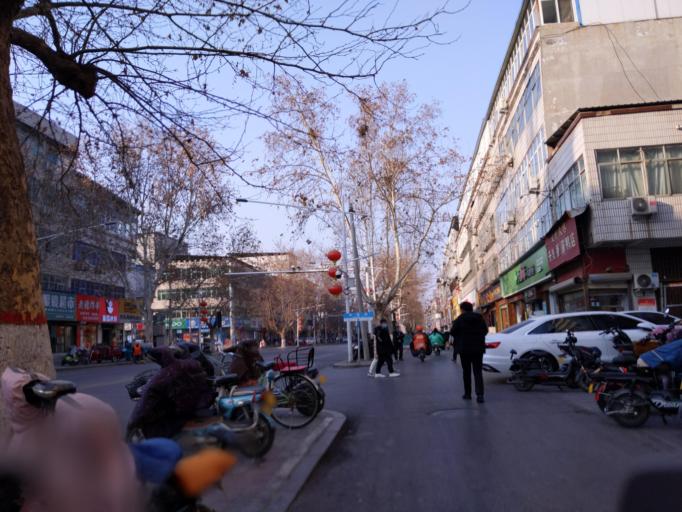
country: CN
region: Henan Sheng
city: Puyang
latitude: 35.7681
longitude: 115.0325
